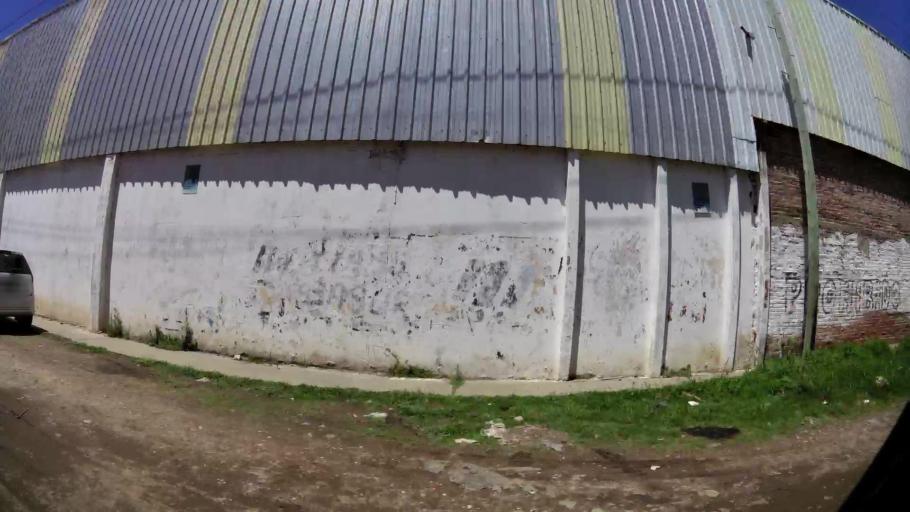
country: AR
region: Buenos Aires
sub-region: Partido de Quilmes
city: Quilmes
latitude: -34.7423
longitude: -58.2745
